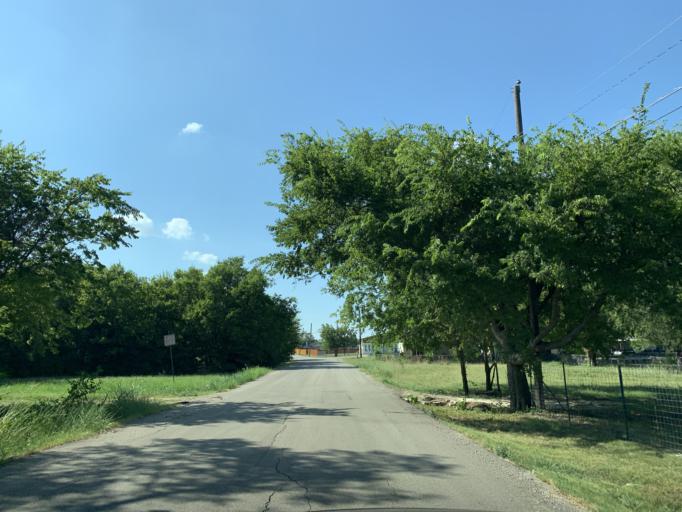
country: US
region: Texas
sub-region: Dallas County
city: Hutchins
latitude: 32.6564
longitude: -96.7696
